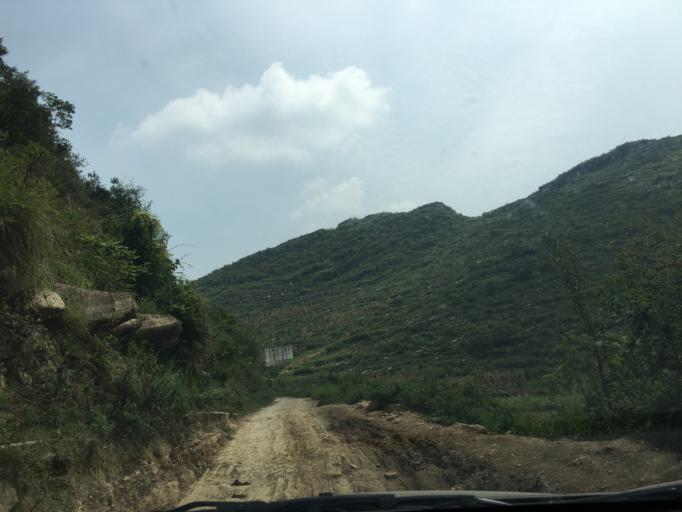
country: CN
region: Guizhou Sheng
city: Anshun
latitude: 25.5987
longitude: 105.6646
